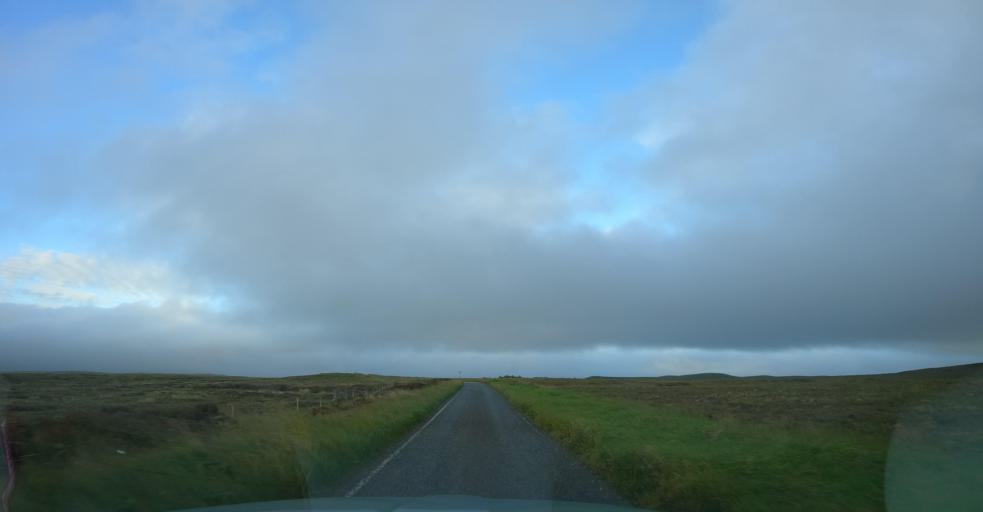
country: GB
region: Scotland
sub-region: Eilean Siar
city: Stornoway
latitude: 58.2031
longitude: -6.2408
